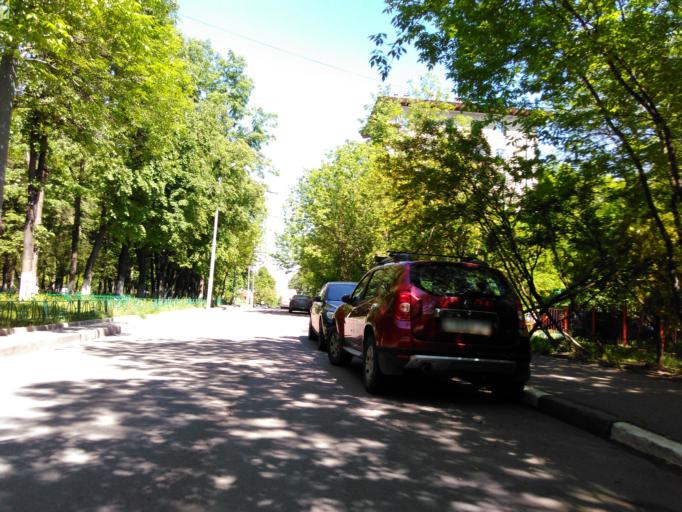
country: RU
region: Moskovskaya
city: Semenovskoye
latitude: 55.6884
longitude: 37.5411
